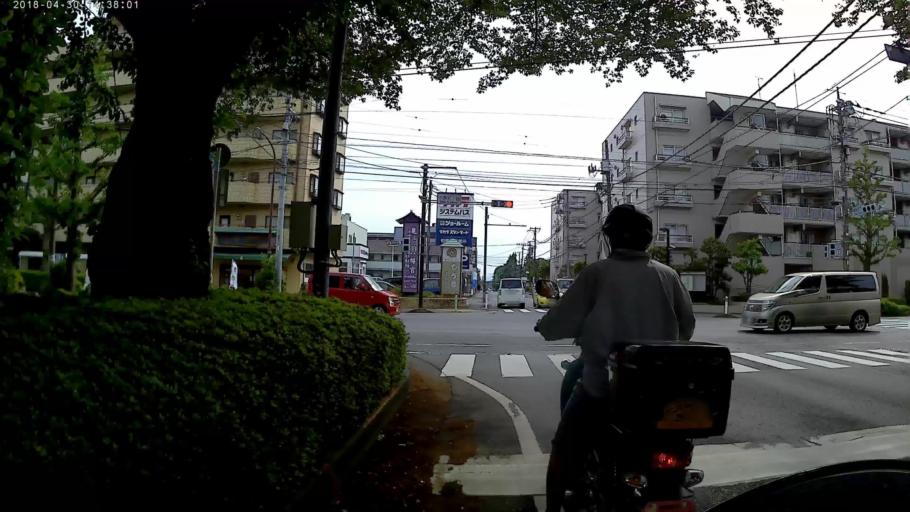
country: JP
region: Kanagawa
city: Zama
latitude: 35.5708
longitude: 139.3686
